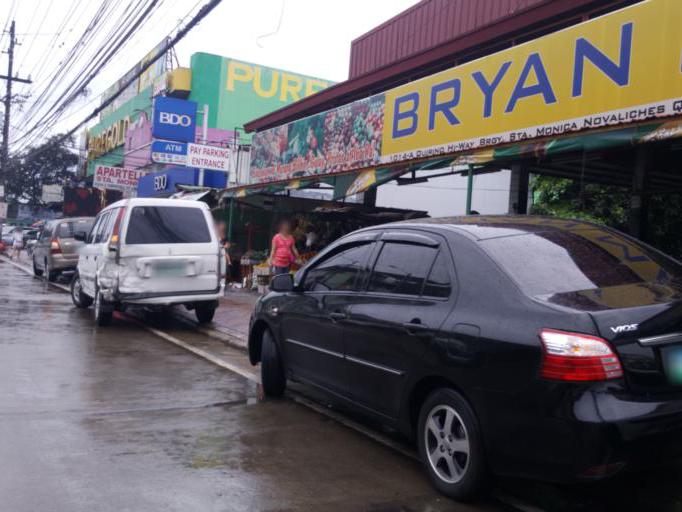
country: PH
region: Calabarzon
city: Bagong Pagasa
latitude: 14.7238
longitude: 121.0414
